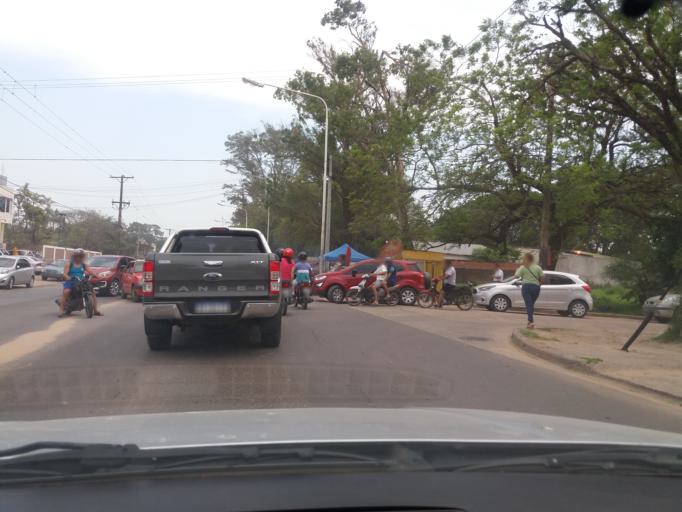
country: AR
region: Corrientes
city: Corrientes
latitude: -27.5061
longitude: -58.8110
